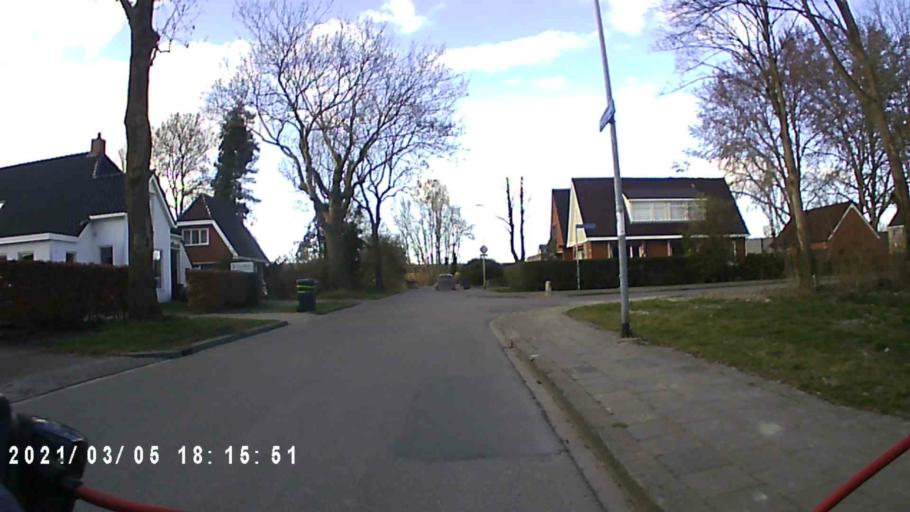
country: NL
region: Groningen
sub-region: Gemeente Groningen
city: Oosterpark
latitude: 53.2334
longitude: 6.5891
